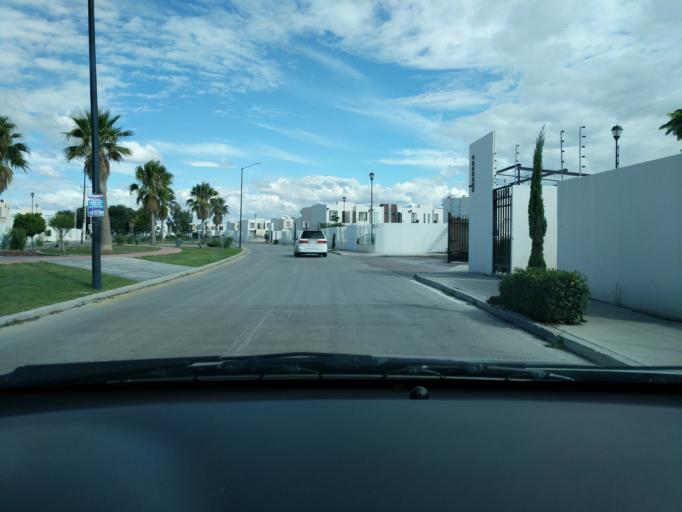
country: MX
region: Queretaro
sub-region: El Marques
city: La Loma
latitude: 20.5863
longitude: -100.2584
